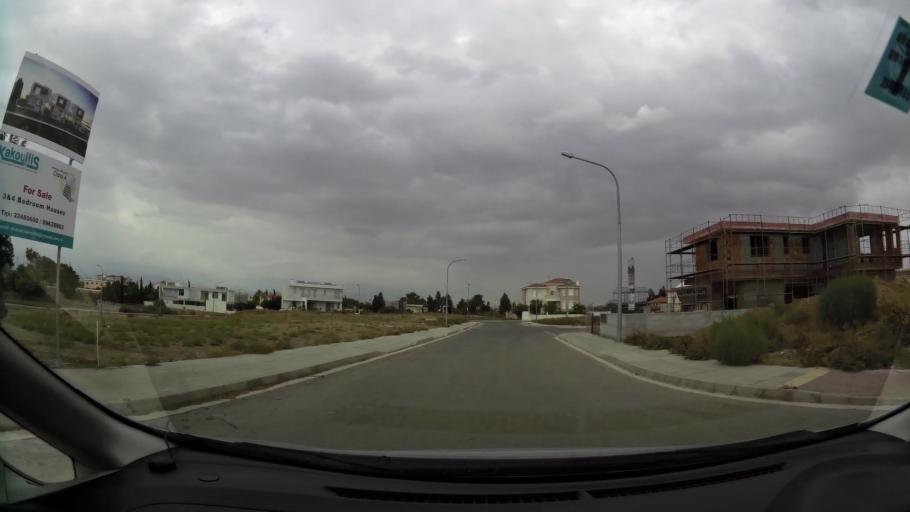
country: CY
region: Lefkosia
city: Geri
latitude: 35.1100
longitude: 33.3918
